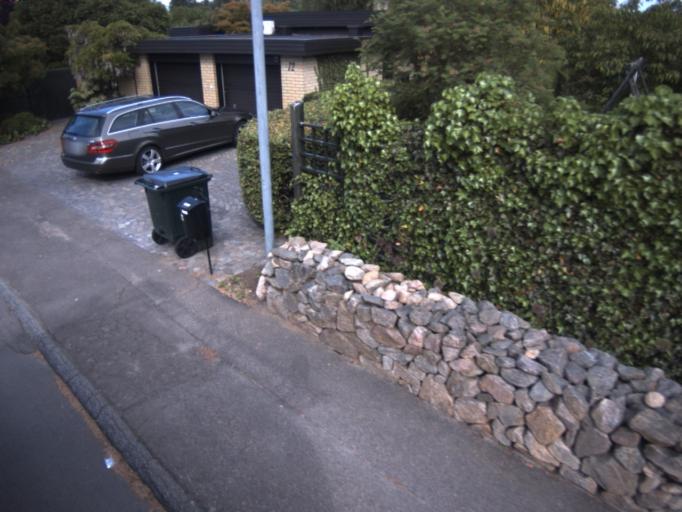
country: SE
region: Skane
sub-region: Helsingborg
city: Helsingborg
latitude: 56.0894
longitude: 12.6557
